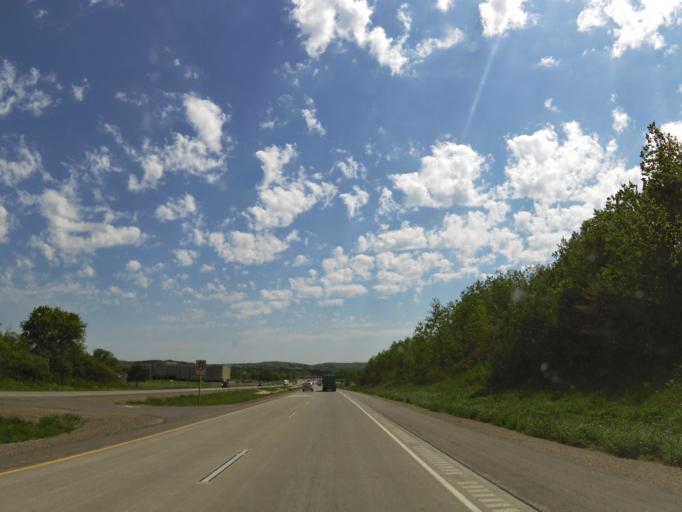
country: US
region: Wisconsin
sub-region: Eau Claire County
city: Altoona
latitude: 44.7655
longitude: -91.4356
